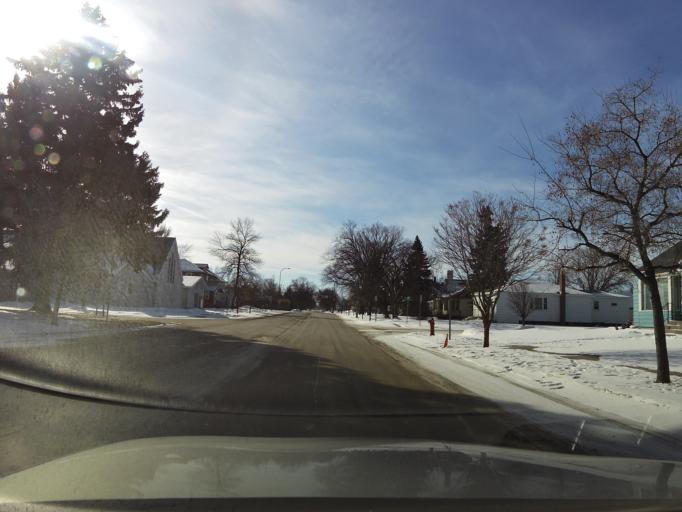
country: US
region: North Dakota
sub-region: Walsh County
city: Grafton
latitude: 48.4139
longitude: -97.4112
